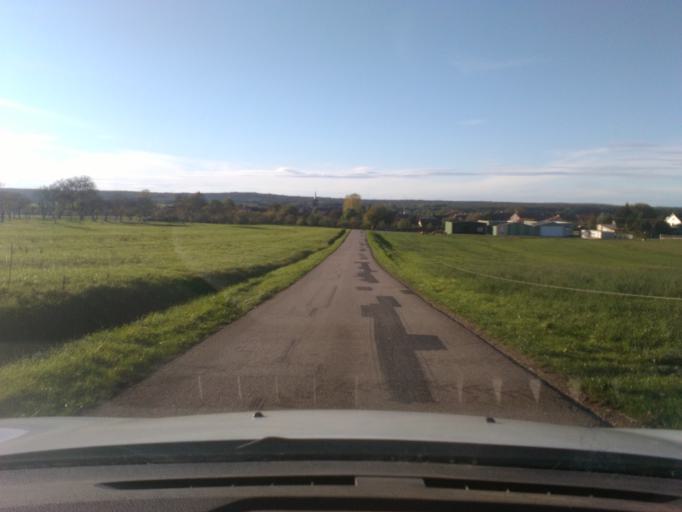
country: FR
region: Lorraine
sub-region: Departement des Vosges
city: Rambervillers
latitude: 48.2917
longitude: 6.6124
